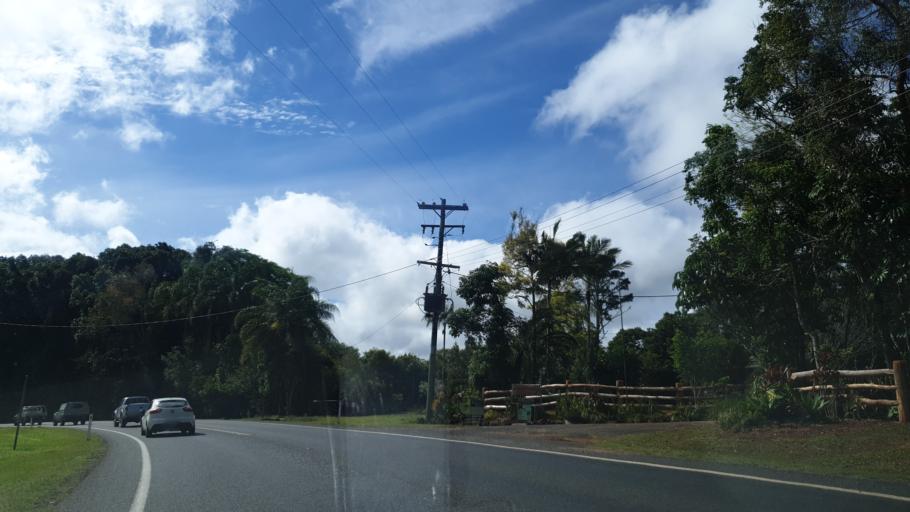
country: AU
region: Queensland
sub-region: Tablelands
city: Atherton
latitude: -17.3551
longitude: 145.5842
